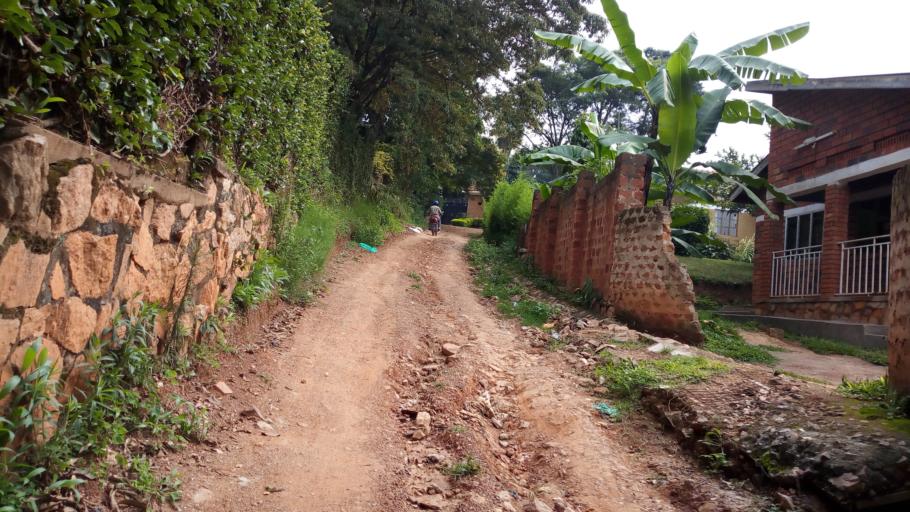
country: UG
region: Central Region
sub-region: Wakiso District
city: Kireka
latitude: 0.3143
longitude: 32.6469
